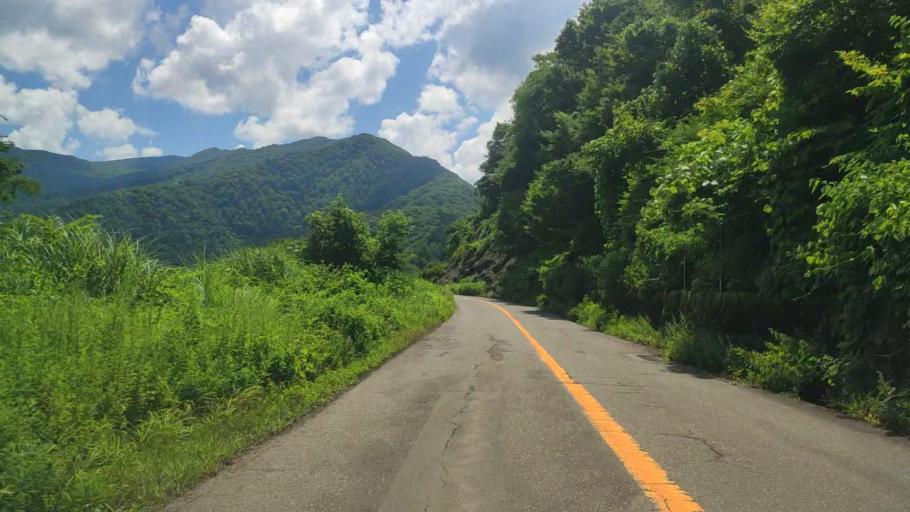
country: JP
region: Fukui
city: Ono
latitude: 35.9143
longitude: 136.5292
